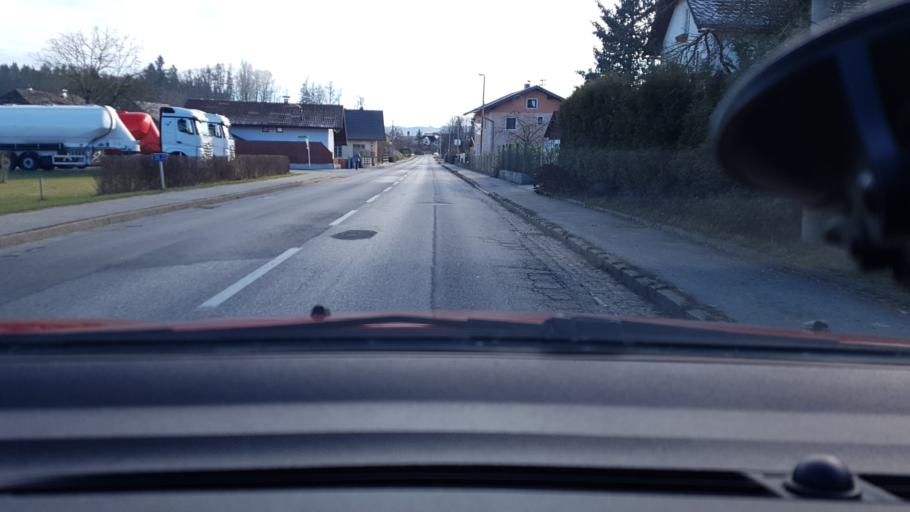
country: AT
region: Salzburg
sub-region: Politischer Bezirk Salzburg-Umgebung
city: Dorfbeuern
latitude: 48.0510
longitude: 12.9855
